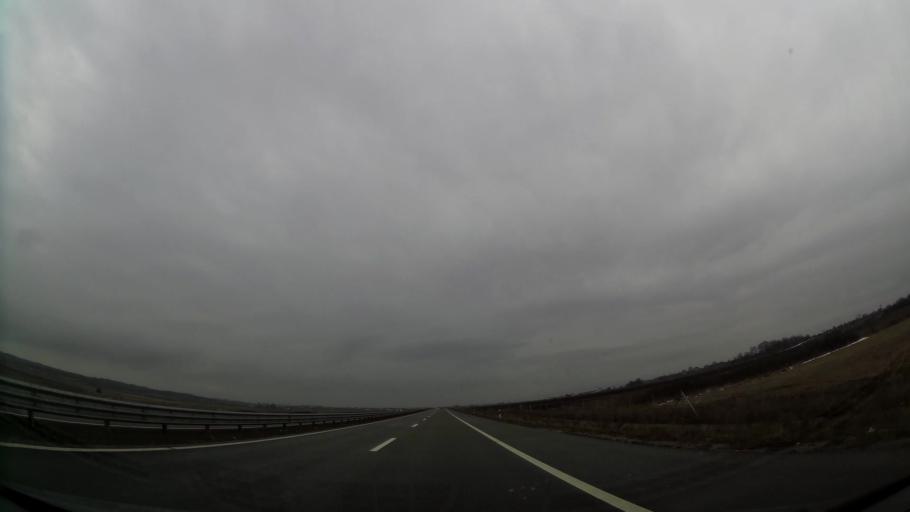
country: XK
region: Ferizaj
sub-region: Komuna e Ferizajt
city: Ferizaj
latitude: 42.4279
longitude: 21.2000
